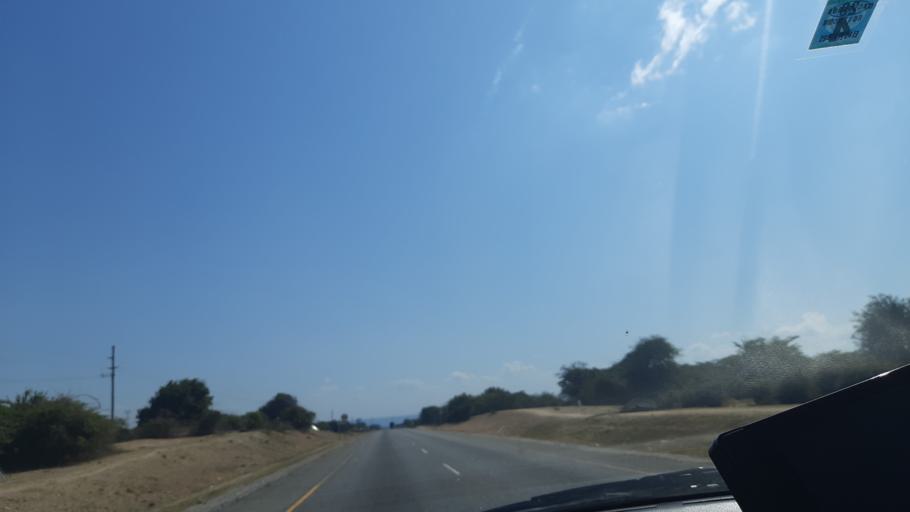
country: TZ
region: Singida
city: Kintinku
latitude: -5.8798
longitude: 35.1293
